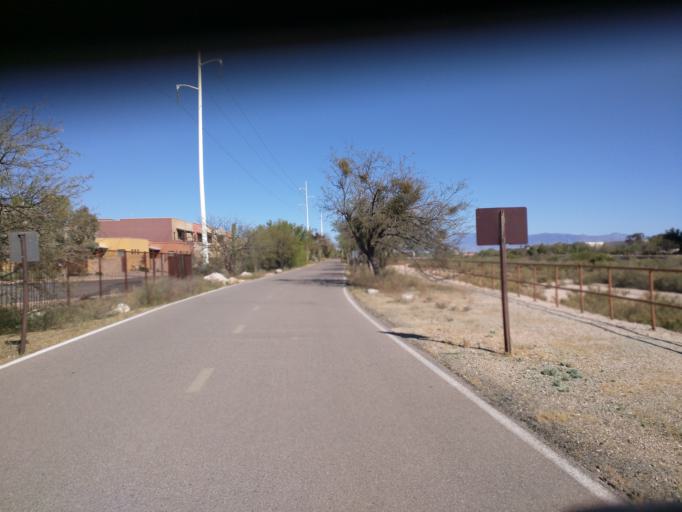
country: US
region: Arizona
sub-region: Pima County
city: Flowing Wells
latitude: 32.2901
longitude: -110.9689
